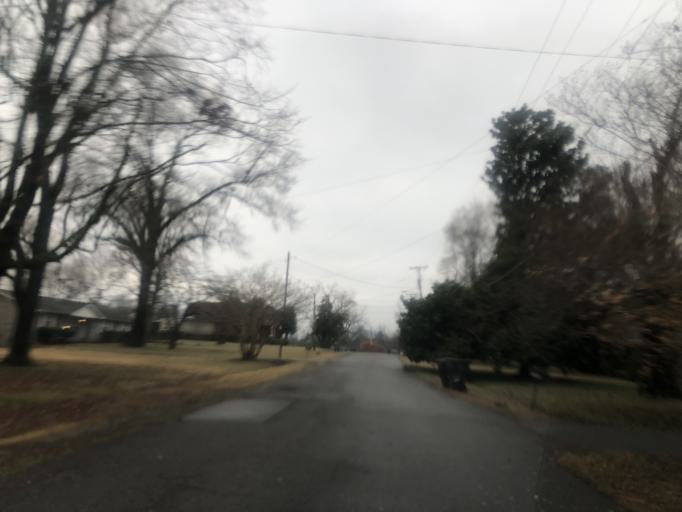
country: US
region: Tennessee
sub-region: Davidson County
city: Lakewood
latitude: 36.1672
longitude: -86.6850
